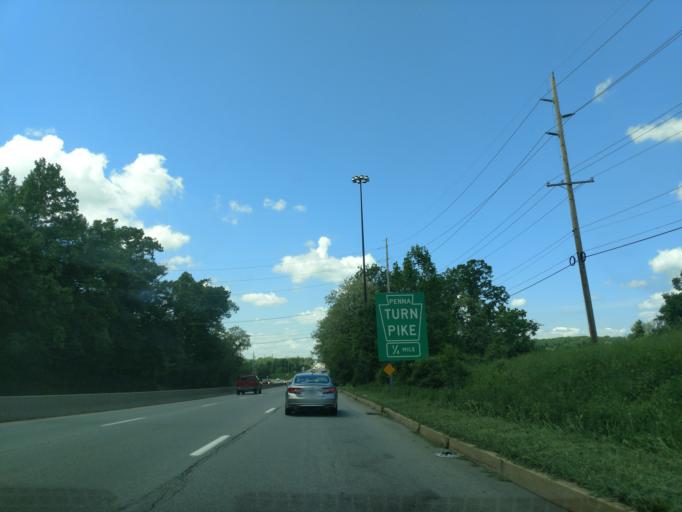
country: US
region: Pennsylvania
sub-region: Chester County
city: Exton
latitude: 40.0589
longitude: -75.6646
